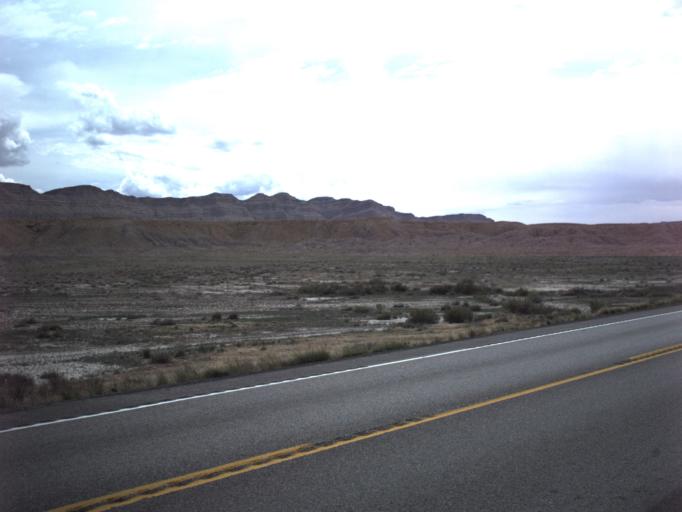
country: US
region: Utah
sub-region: Carbon County
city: East Carbon City
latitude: 39.3113
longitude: -110.3612
